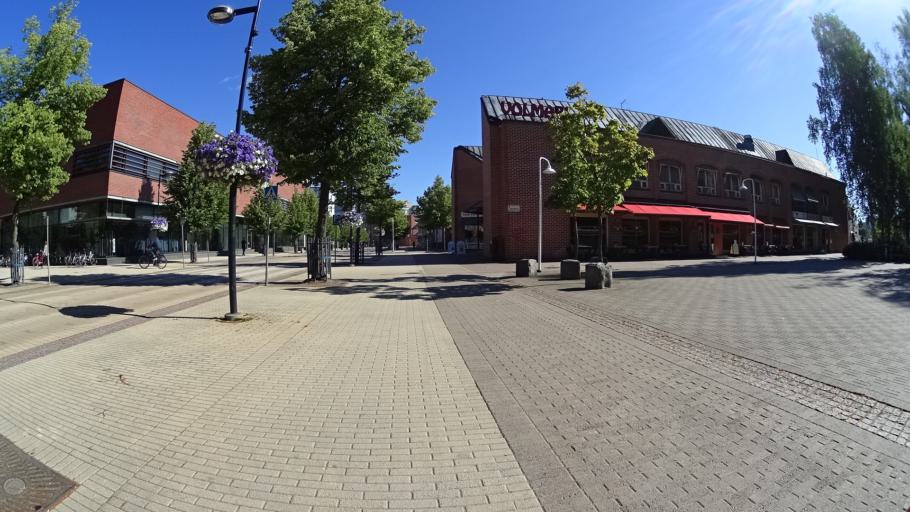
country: FI
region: Uusimaa
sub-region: Helsinki
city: Kerava
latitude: 60.4049
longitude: 25.1031
